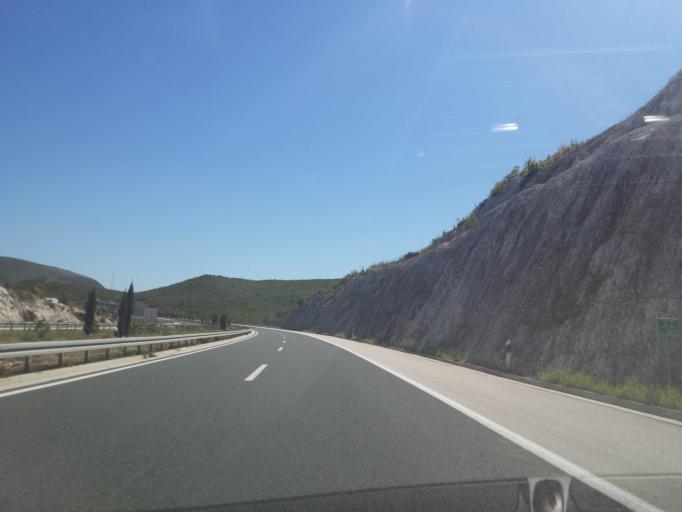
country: HR
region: Splitsko-Dalmatinska
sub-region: Grad Omis
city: Omis
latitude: 43.4795
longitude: 16.8095
